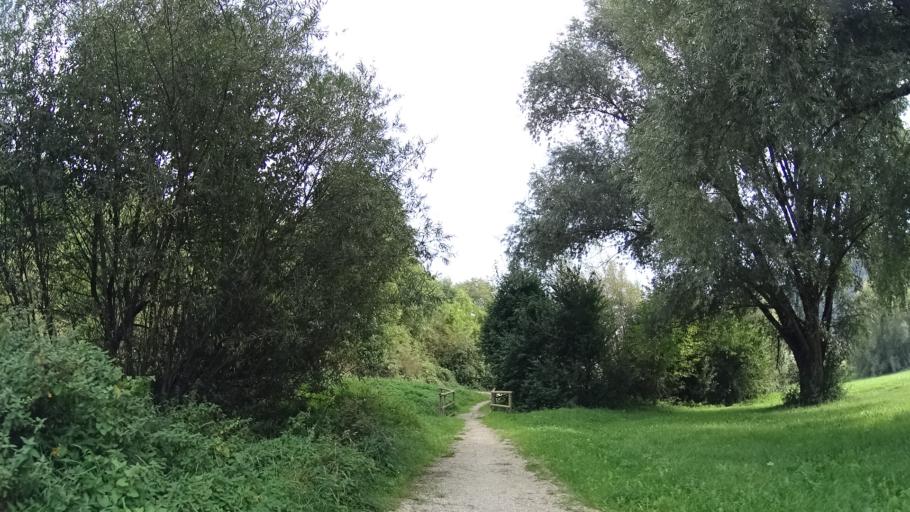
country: DE
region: Bavaria
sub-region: Upper Bavaria
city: Mindelstetten
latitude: 48.8990
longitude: 11.6455
